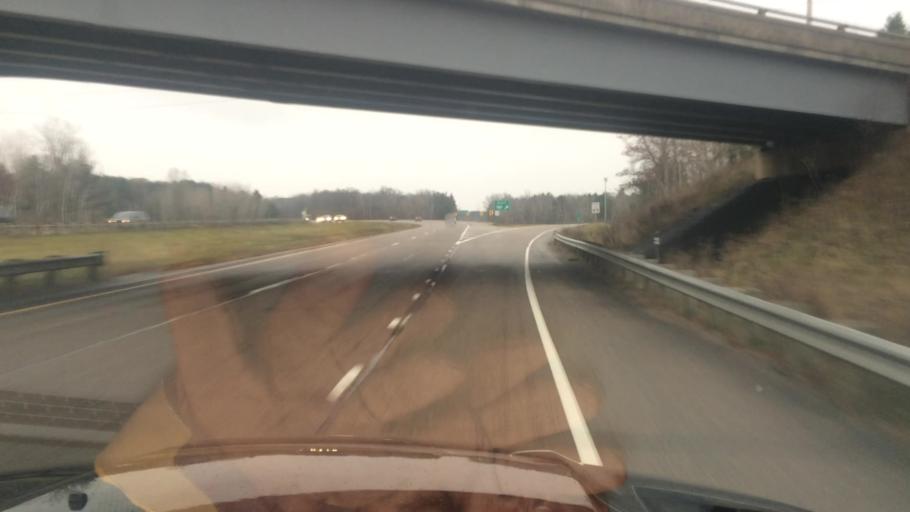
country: US
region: Wisconsin
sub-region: Portage County
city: Stevens Point
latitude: 44.5525
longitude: -89.5841
